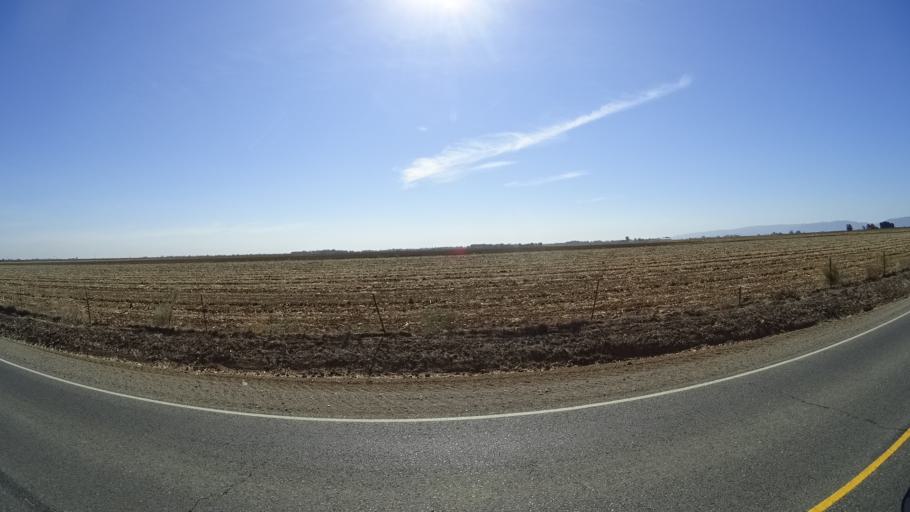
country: US
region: California
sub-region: Yolo County
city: Woodland
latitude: 38.6197
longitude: -121.8466
